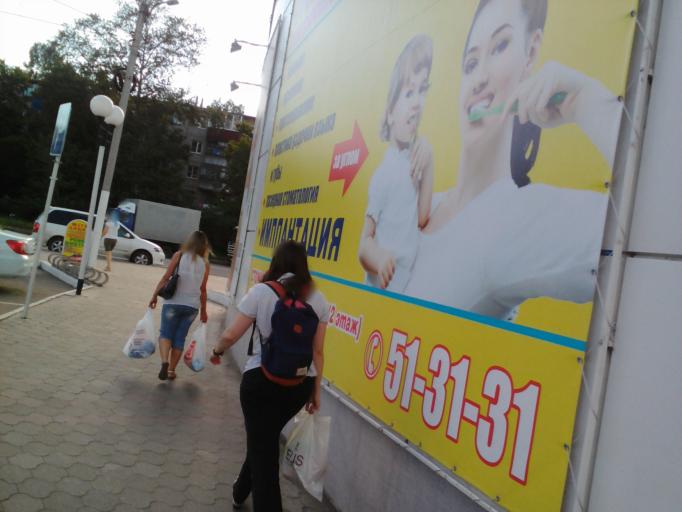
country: RU
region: Kursk
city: Voroshnevo
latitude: 51.6694
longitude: 36.0742
